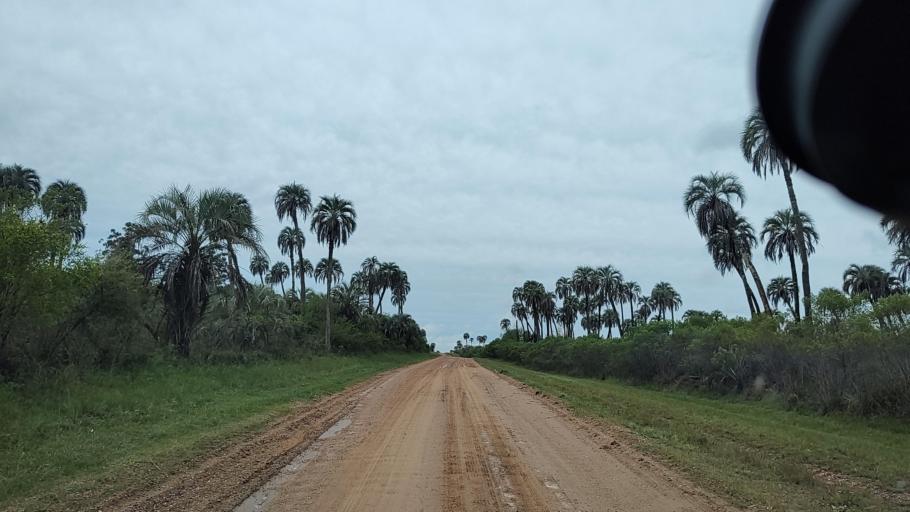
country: AR
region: Entre Rios
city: Ubajay
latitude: -31.8537
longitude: -58.2932
